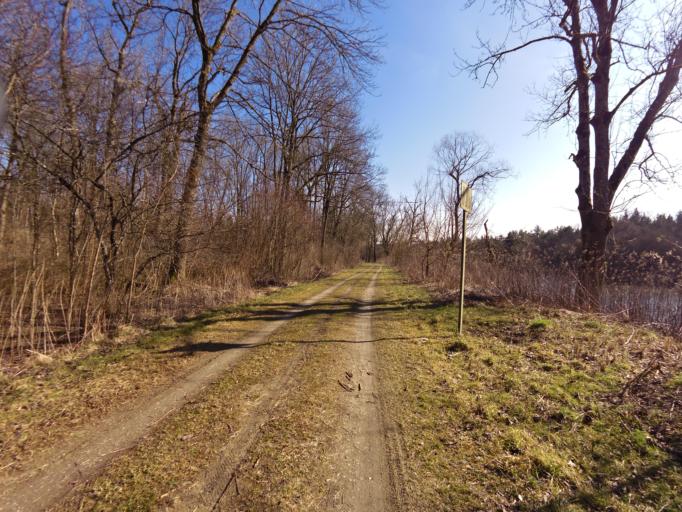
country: DE
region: Bavaria
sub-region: Upper Bavaria
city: Wang
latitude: 48.4991
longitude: 11.9798
